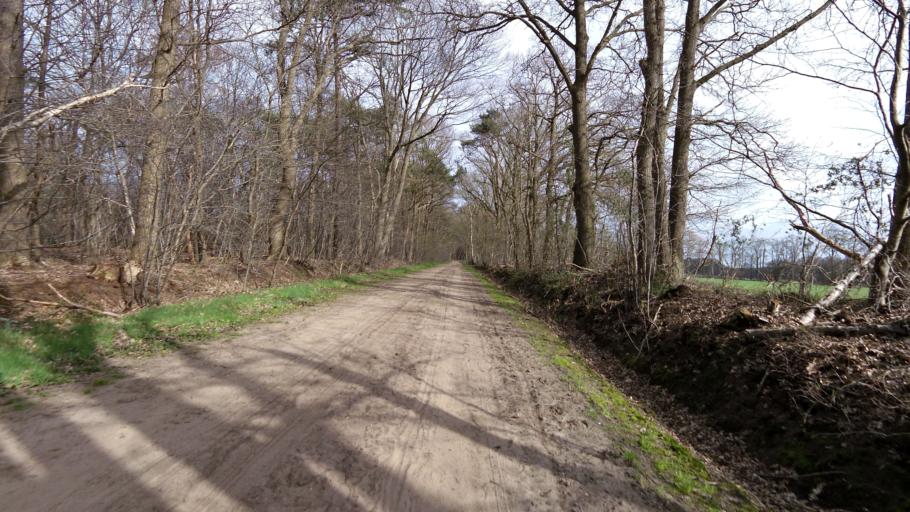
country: NL
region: Gelderland
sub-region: Gemeente Barneveld
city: Voorthuizen
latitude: 52.2175
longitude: 5.5766
